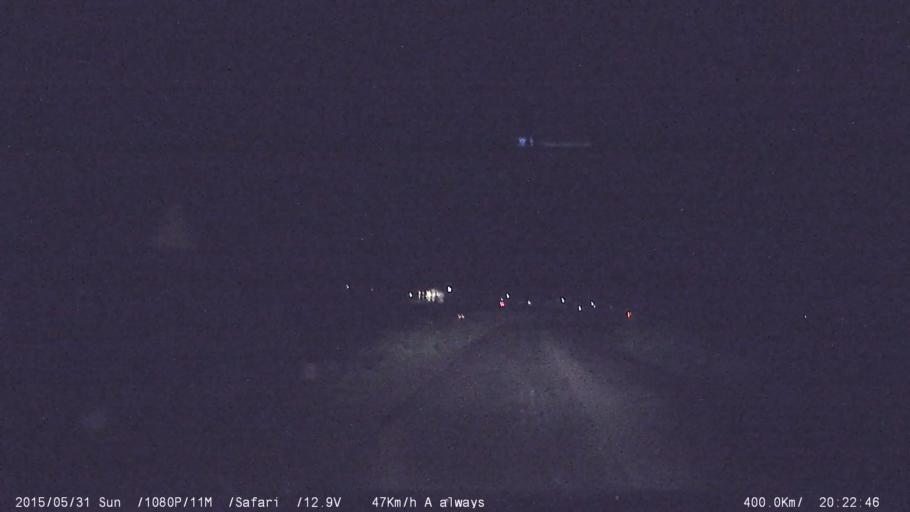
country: IN
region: Karnataka
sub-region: Mandya
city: Malavalli
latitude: 12.4262
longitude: 77.2212
